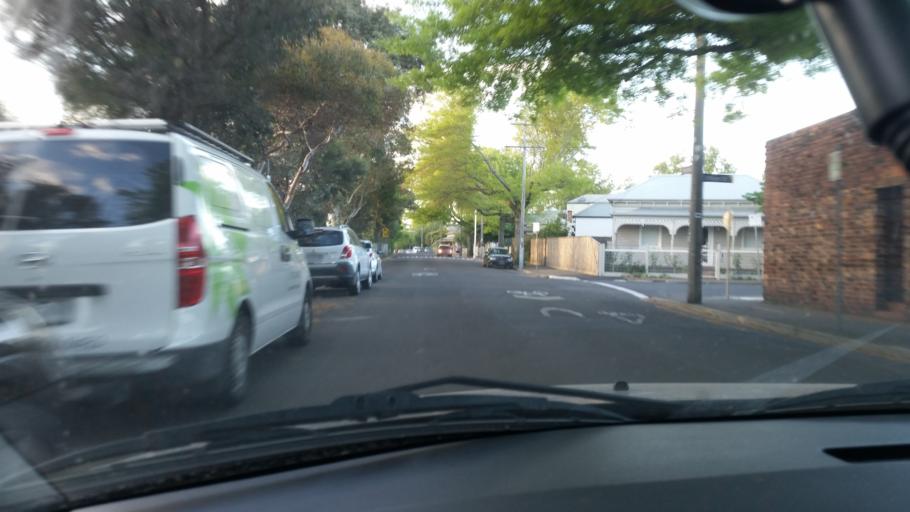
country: AU
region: Victoria
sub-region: Moonee Valley
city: Flemington
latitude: -37.7848
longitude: 144.9286
